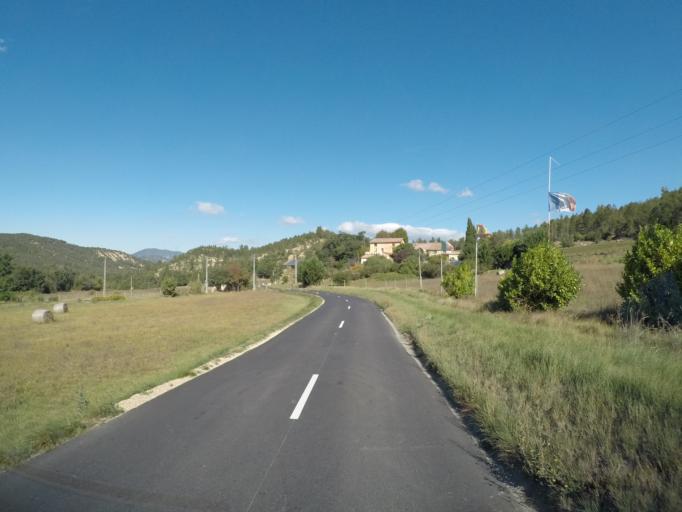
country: FR
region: Provence-Alpes-Cote d'Azur
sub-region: Departement des Alpes-de-Haute-Provence
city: Mallemoisson
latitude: 44.0204
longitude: 6.1790
